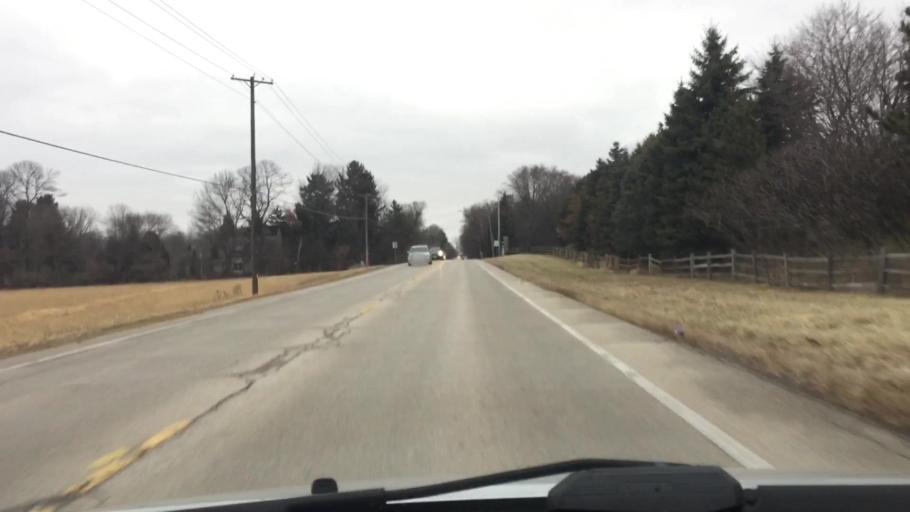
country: US
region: Wisconsin
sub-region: Waukesha County
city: Nashotah
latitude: 43.0897
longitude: -88.4032
